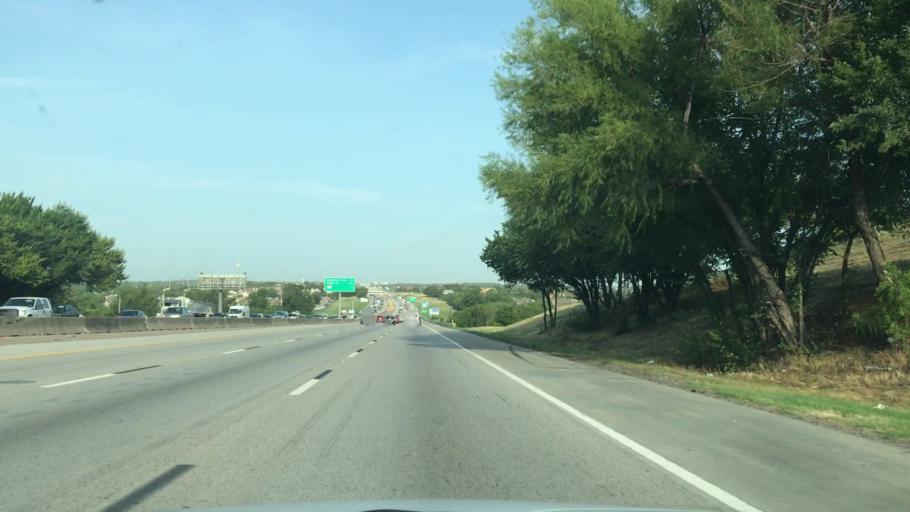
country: US
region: Texas
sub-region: Tarrant County
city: Arlington
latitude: 32.7601
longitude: -97.1465
